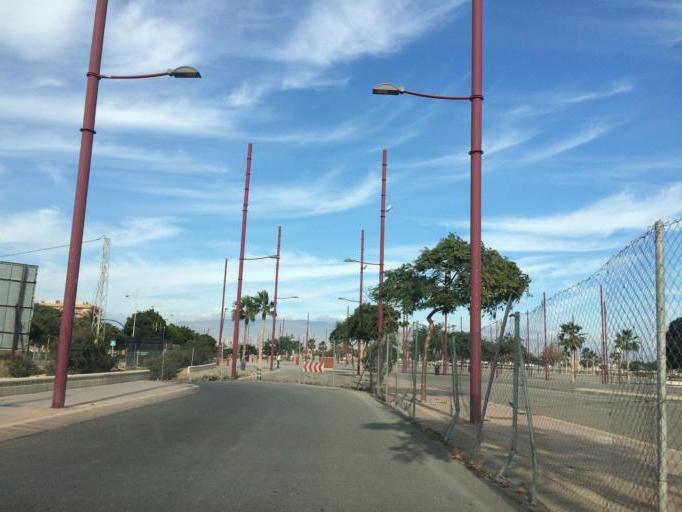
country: ES
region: Andalusia
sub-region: Provincia de Almeria
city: Almeria
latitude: 36.8336
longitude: -2.4323
